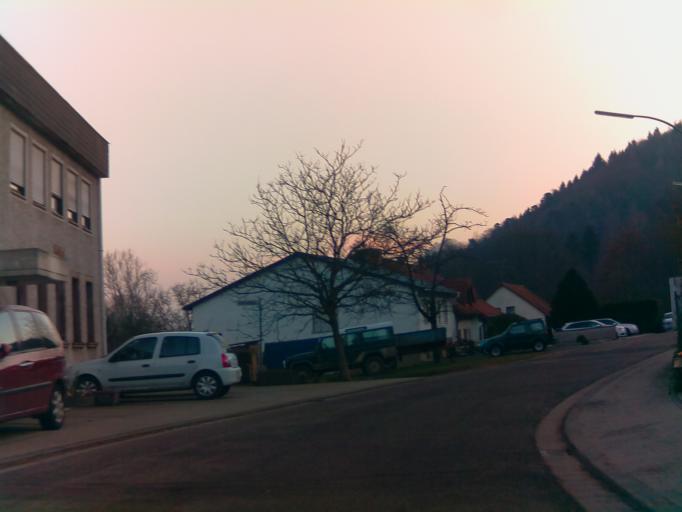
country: DE
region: Saarland
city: Sankt Ingbert
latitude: 49.2548
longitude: 7.1004
